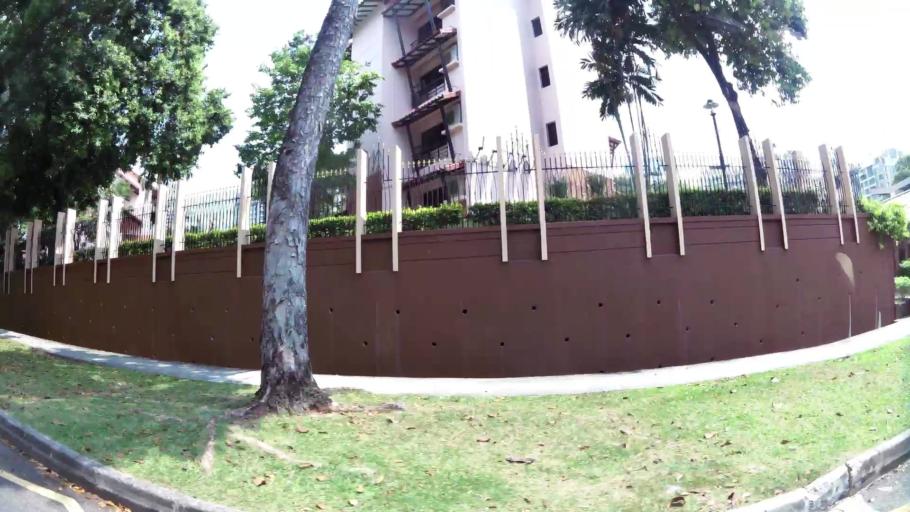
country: SG
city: Singapore
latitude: 1.2949
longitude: 103.8246
